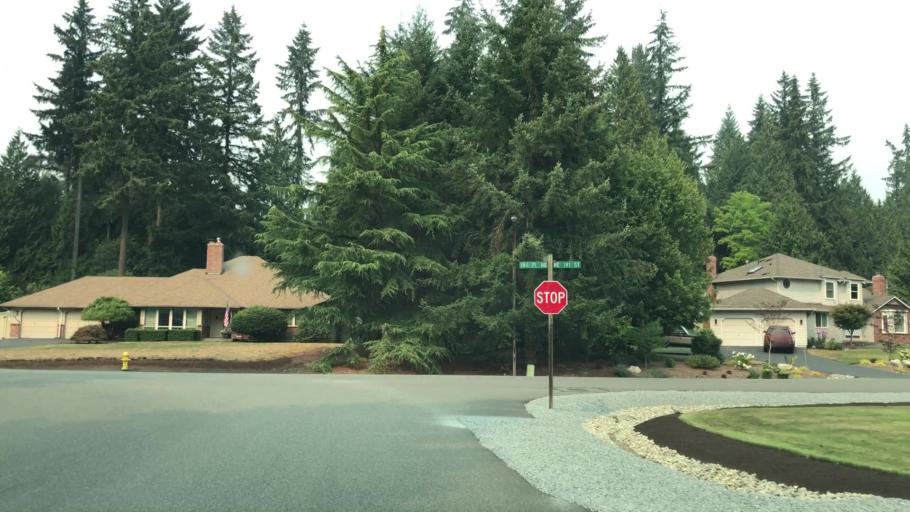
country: US
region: Washington
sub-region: King County
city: Cottage Lake
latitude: 47.7660
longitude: -122.0908
